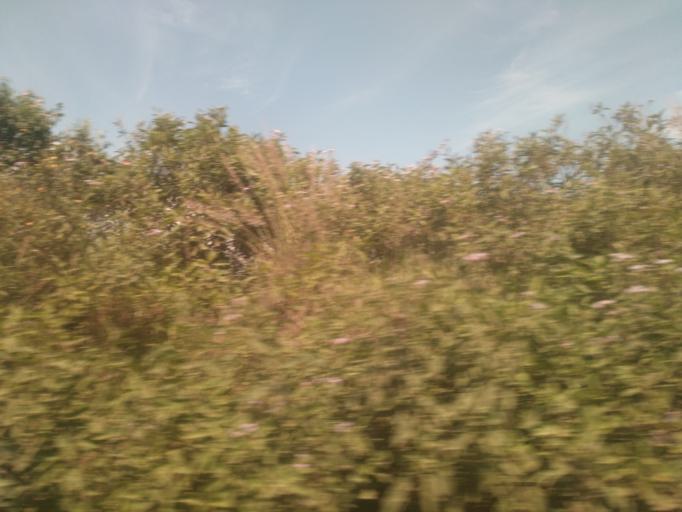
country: UG
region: Central Region
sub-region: Wakiso District
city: Entebbe
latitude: 0.0366
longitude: 32.4310
